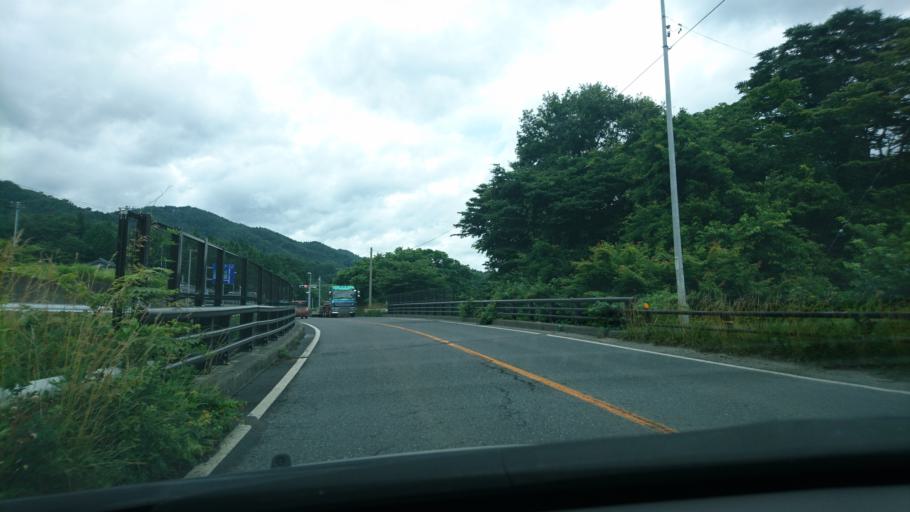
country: JP
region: Iwate
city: Yamada
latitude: 39.4226
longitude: 141.9718
